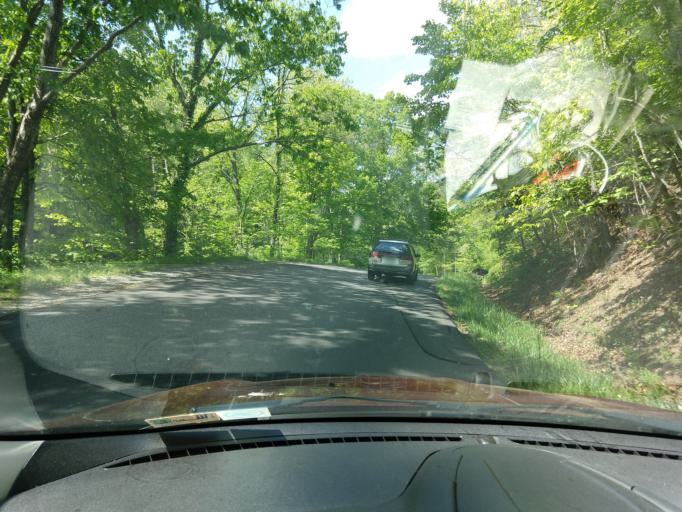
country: US
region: Virginia
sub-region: City of Covington
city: Fairlawn
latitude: 37.6950
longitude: -79.8876
